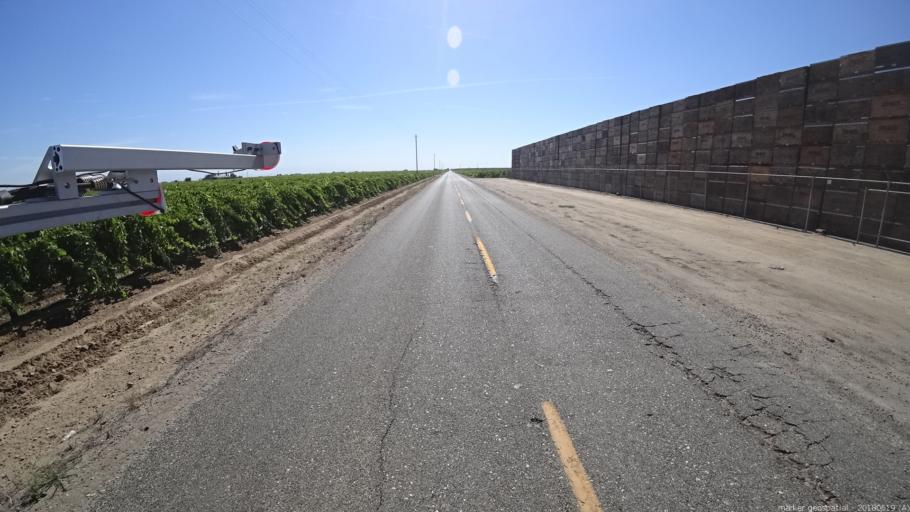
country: US
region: California
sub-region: Fresno County
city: Biola
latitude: 36.8368
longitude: -120.0527
